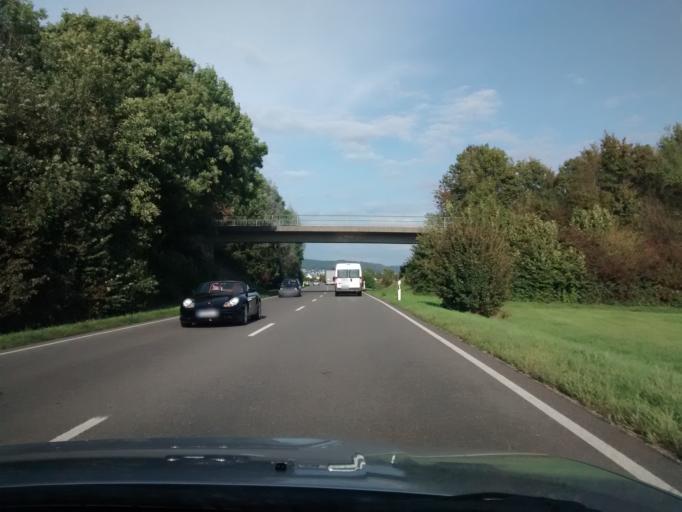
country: DE
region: Baden-Wuerttemberg
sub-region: Freiburg Region
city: Dogern
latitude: 47.6021
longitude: 8.1642
